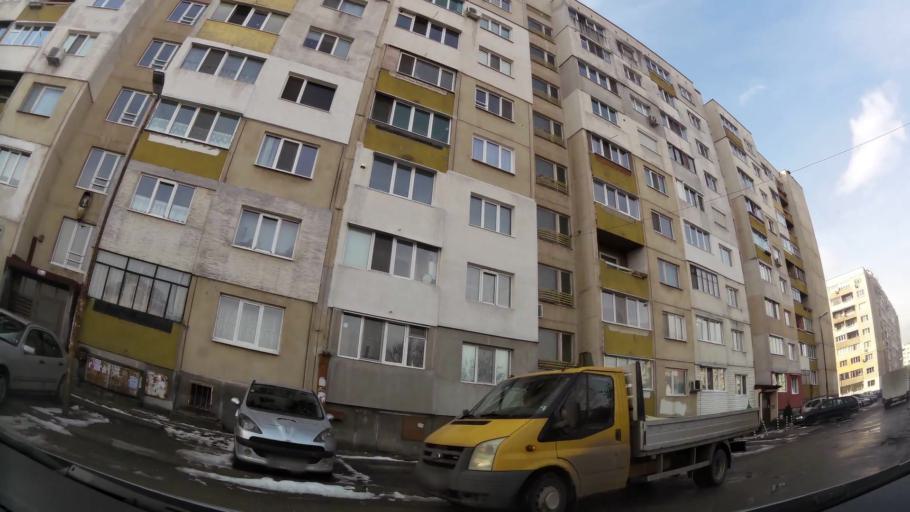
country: BG
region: Sofia-Capital
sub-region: Stolichna Obshtina
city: Sofia
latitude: 42.7208
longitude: 23.2680
